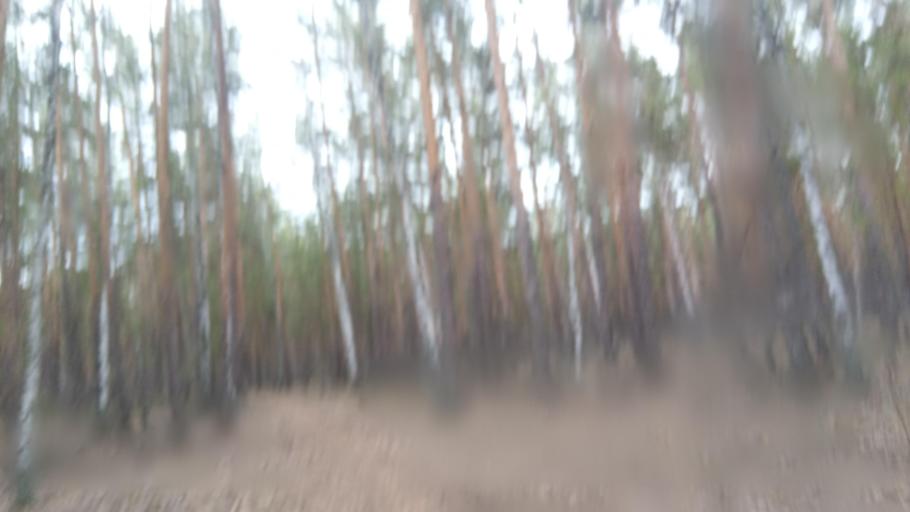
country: RU
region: Chelyabinsk
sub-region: Gorod Chelyabinsk
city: Chelyabinsk
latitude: 55.1331
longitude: 61.3408
